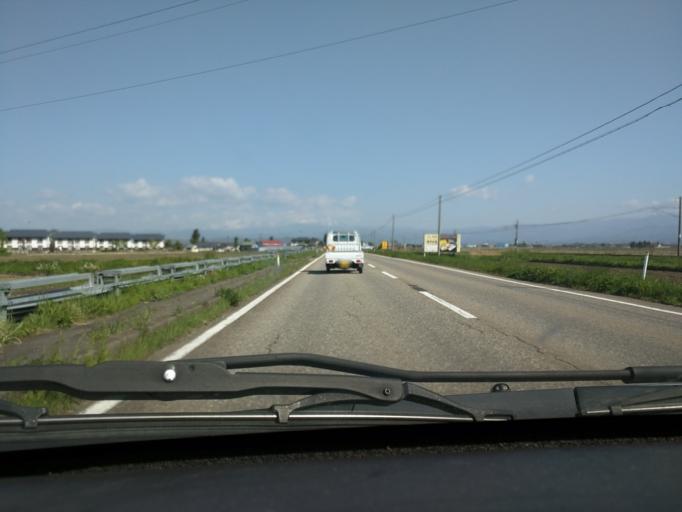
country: JP
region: Fukushima
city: Kitakata
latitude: 37.5756
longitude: 139.8974
